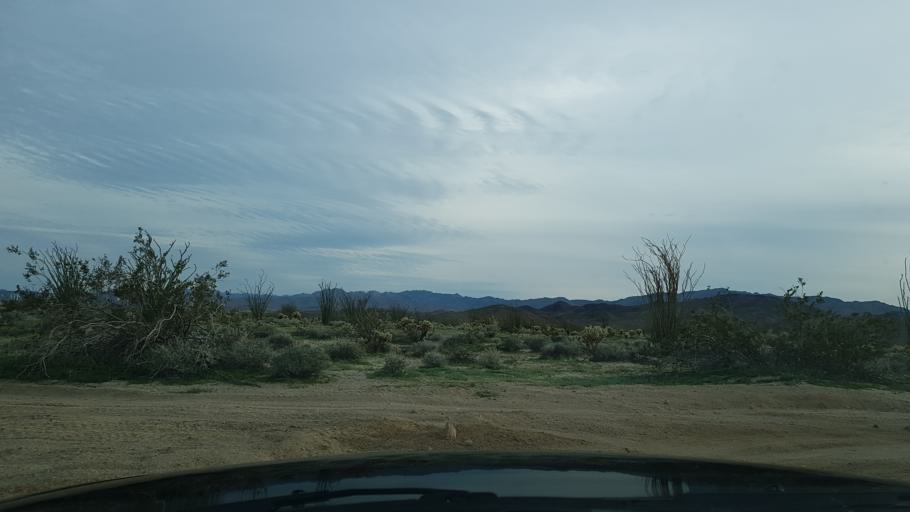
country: MX
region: Baja California
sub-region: Tecate
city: Cereso del Hongo
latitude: 32.8160
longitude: -116.1300
